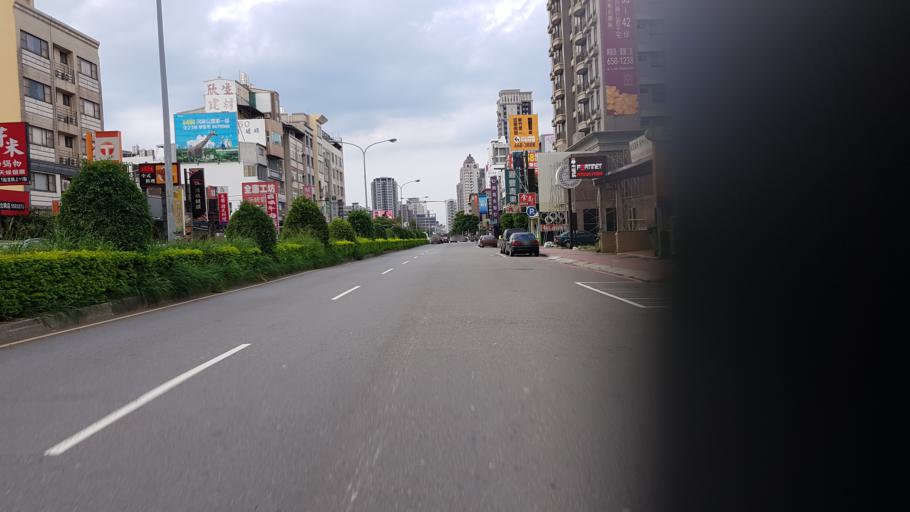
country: TW
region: Taiwan
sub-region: Hsinchu
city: Zhubei
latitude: 24.8121
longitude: 121.0258
